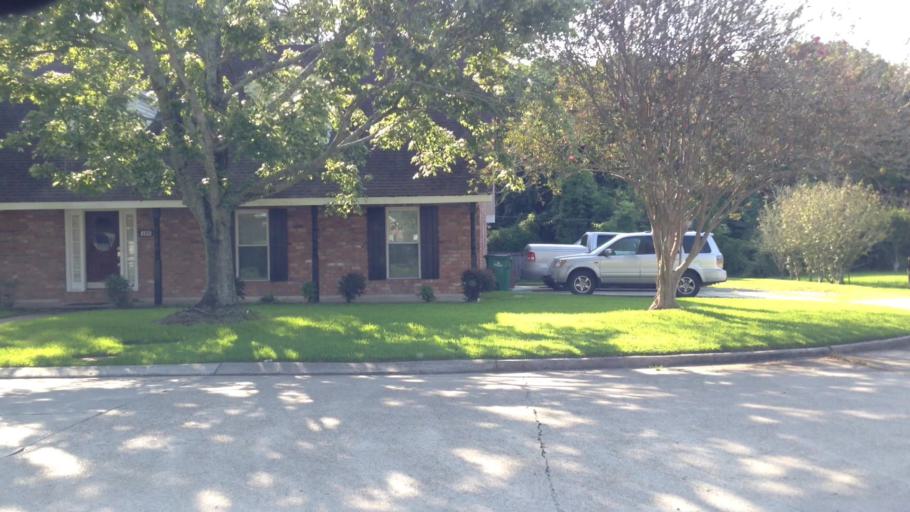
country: US
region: Louisiana
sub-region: Jefferson Parish
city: Jefferson
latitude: 29.9472
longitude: -90.1554
